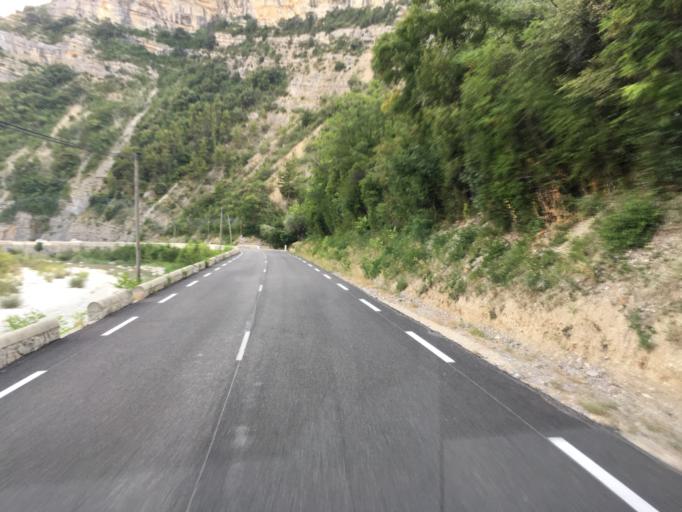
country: FR
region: Rhone-Alpes
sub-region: Departement de la Drome
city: Buis-les-Baronnies
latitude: 44.4308
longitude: 5.2772
